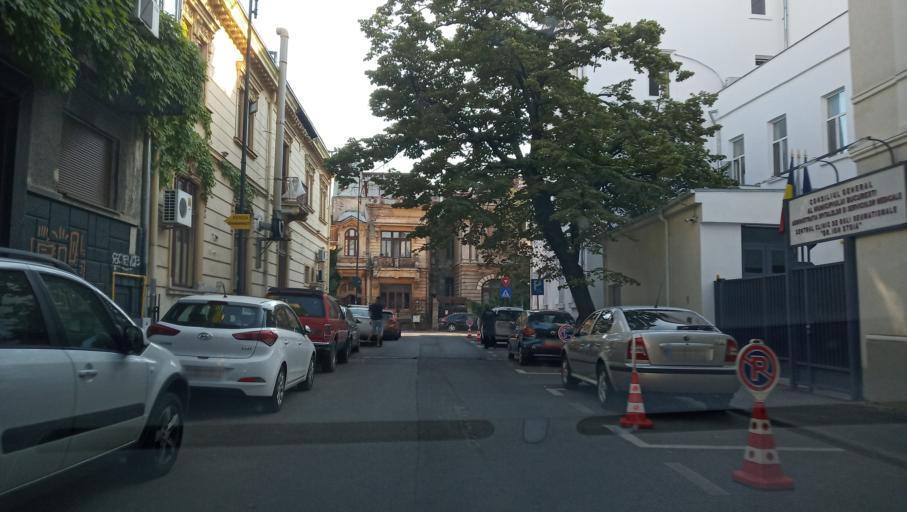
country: RO
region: Bucuresti
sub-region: Municipiul Bucuresti
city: Bucharest
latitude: 44.4413
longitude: 26.1057
